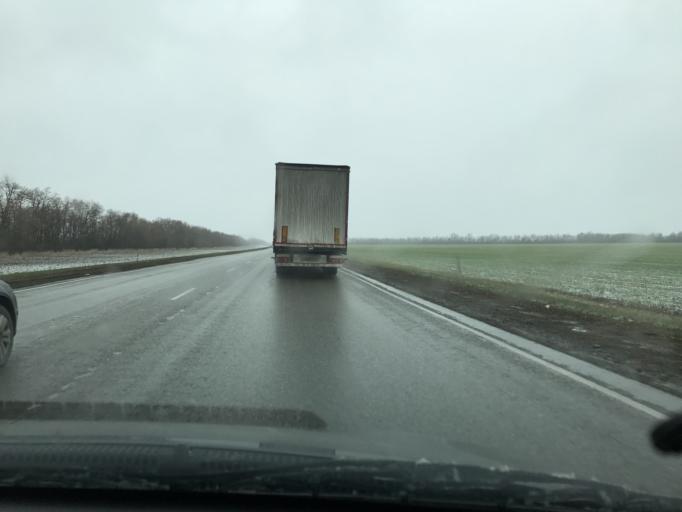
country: RU
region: Rostov
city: Kagal'nitskaya
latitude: 46.8548
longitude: 40.1963
